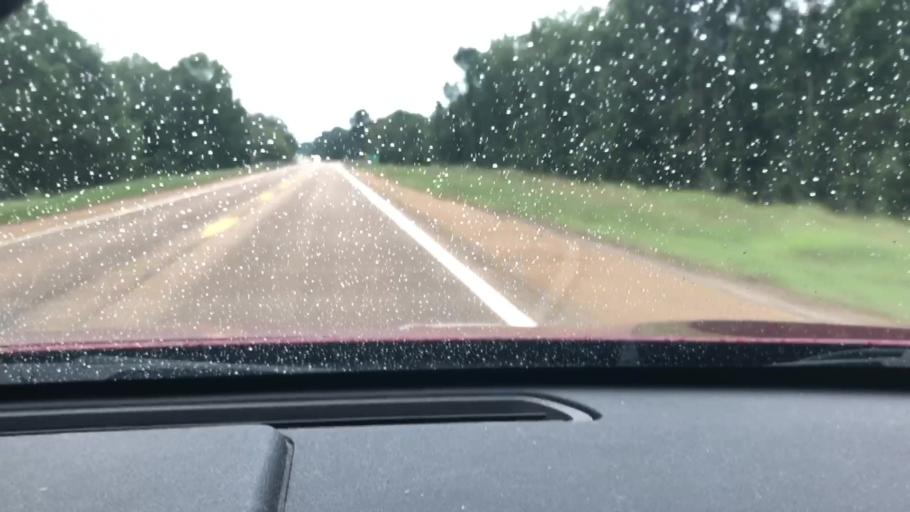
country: US
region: Arkansas
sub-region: Lafayette County
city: Stamps
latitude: 33.3588
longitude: -93.4120
